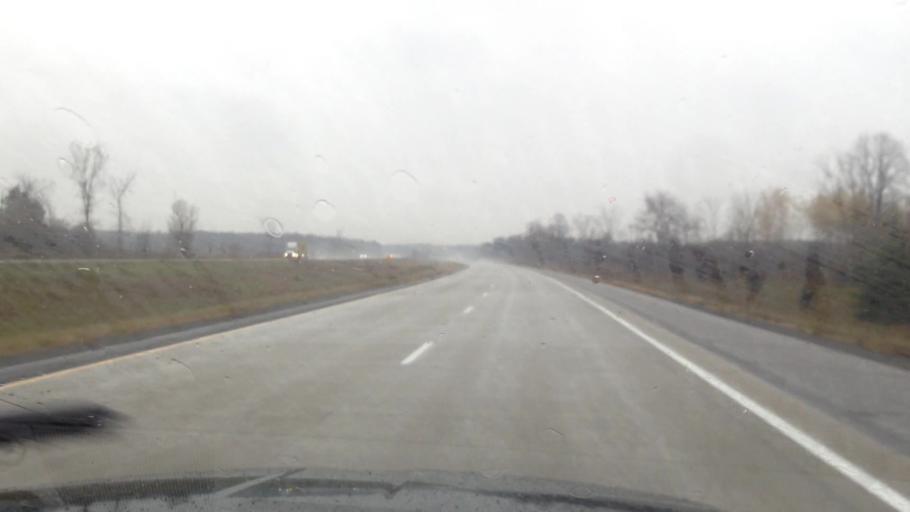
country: CA
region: Ontario
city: Hawkesbury
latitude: 45.3834
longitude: -74.7985
